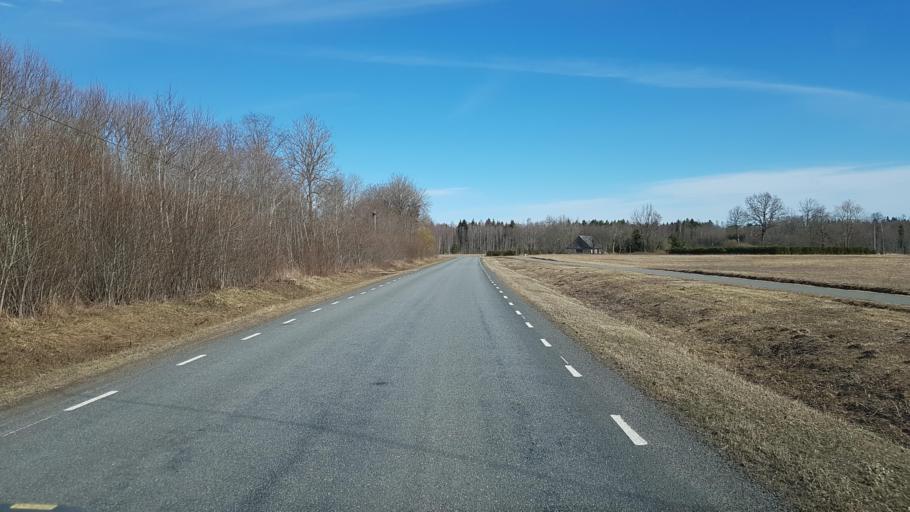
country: EE
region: Harju
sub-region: Nissi vald
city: Riisipere
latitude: 59.2377
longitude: 24.2438
